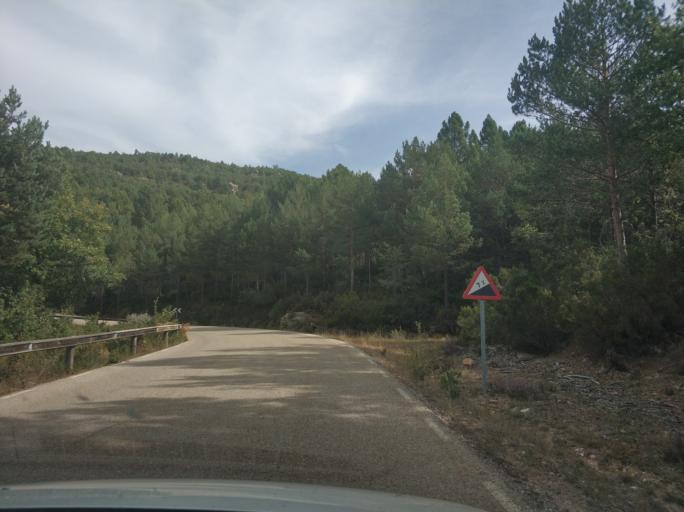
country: ES
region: Castille and Leon
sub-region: Provincia de Soria
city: Duruelo de la Sierra
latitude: 41.9001
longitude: -2.9394
